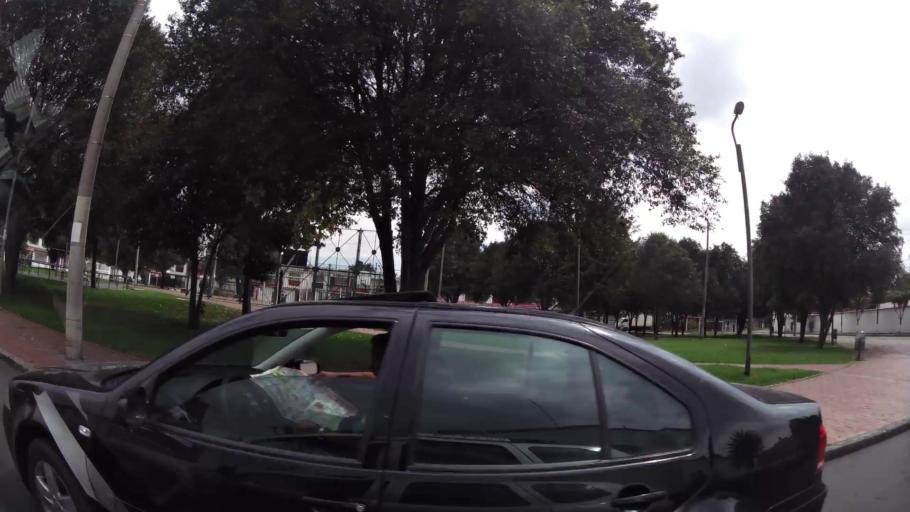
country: CO
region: Bogota D.C.
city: Barrio San Luis
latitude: 4.6851
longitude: -74.0681
